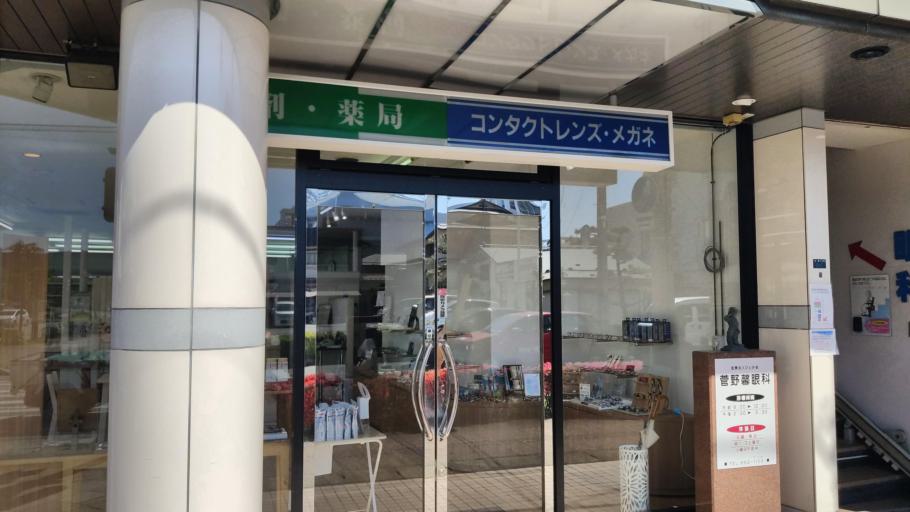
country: JP
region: Yamagata
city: Tendo
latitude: 38.3597
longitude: 140.3715
